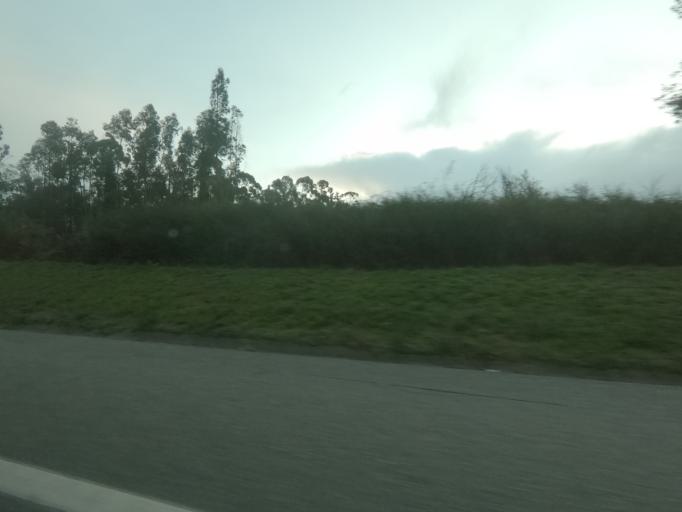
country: PT
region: Braga
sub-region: Vila Verde
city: Prado
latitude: 41.6562
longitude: -8.5487
